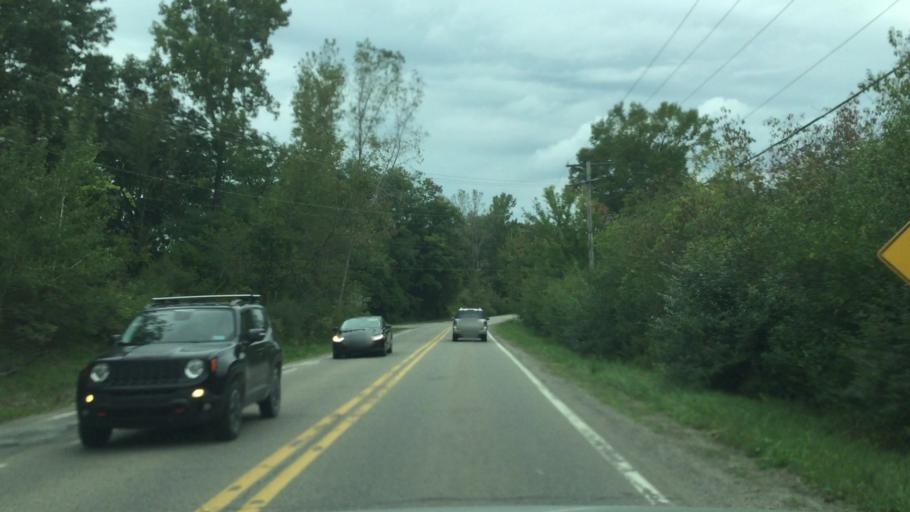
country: US
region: Michigan
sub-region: Livingston County
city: Brighton
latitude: 42.4649
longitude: -83.8337
